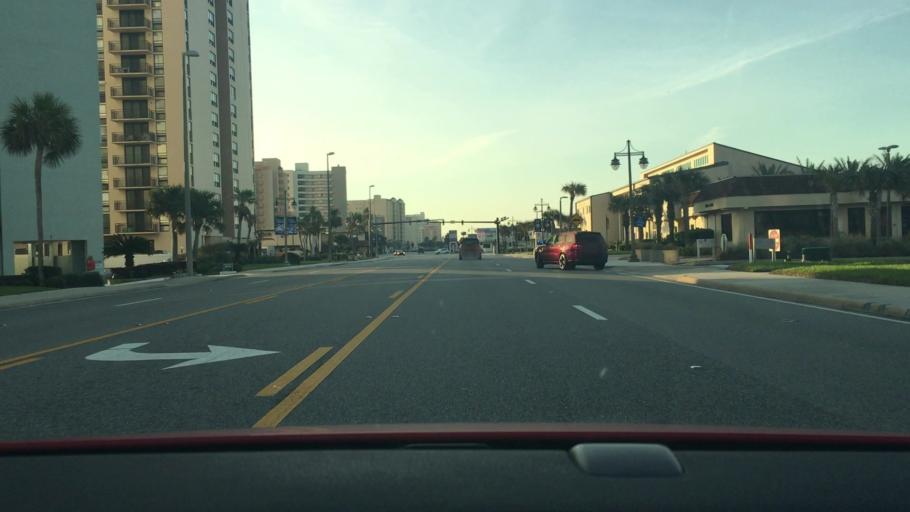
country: US
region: Florida
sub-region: Volusia County
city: Daytona Beach Shores
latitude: 29.1670
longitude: -80.9777
